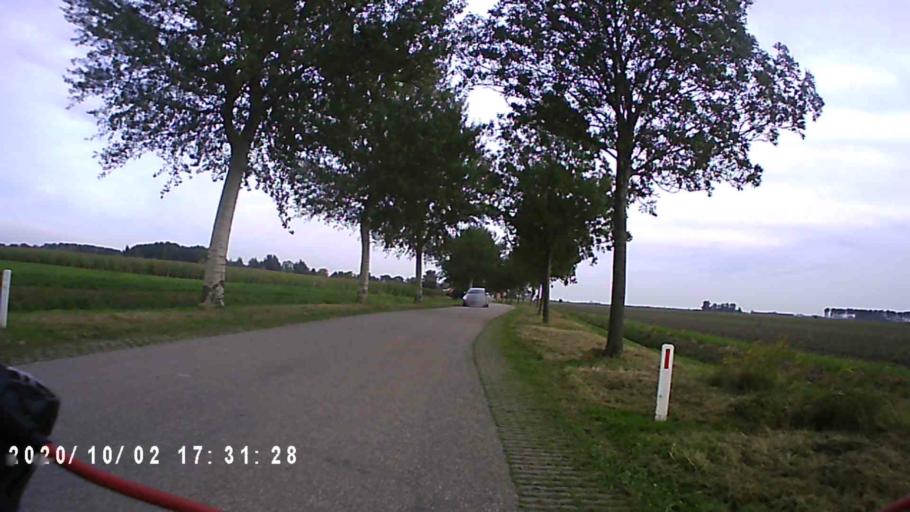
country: NL
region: Groningen
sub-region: Gemeente De Marne
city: Ulrum
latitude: 53.3363
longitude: 6.3320
